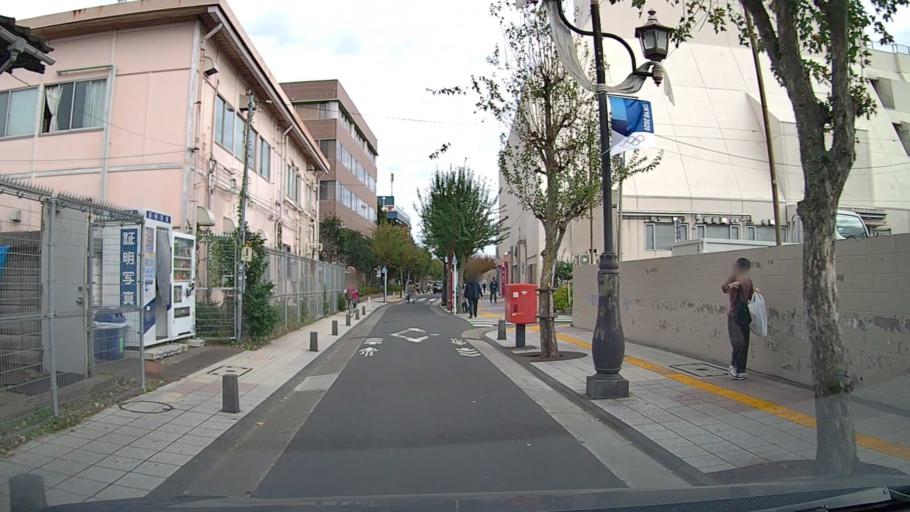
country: JP
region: Tokyo
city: Tokyo
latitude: 35.7050
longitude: 139.6704
